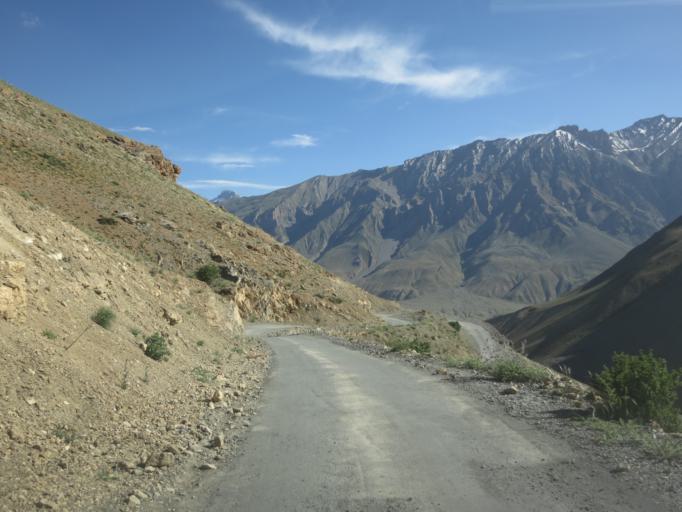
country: IN
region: Himachal Pradesh
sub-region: Kulu
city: Manali
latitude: 32.3233
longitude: 78.0032
